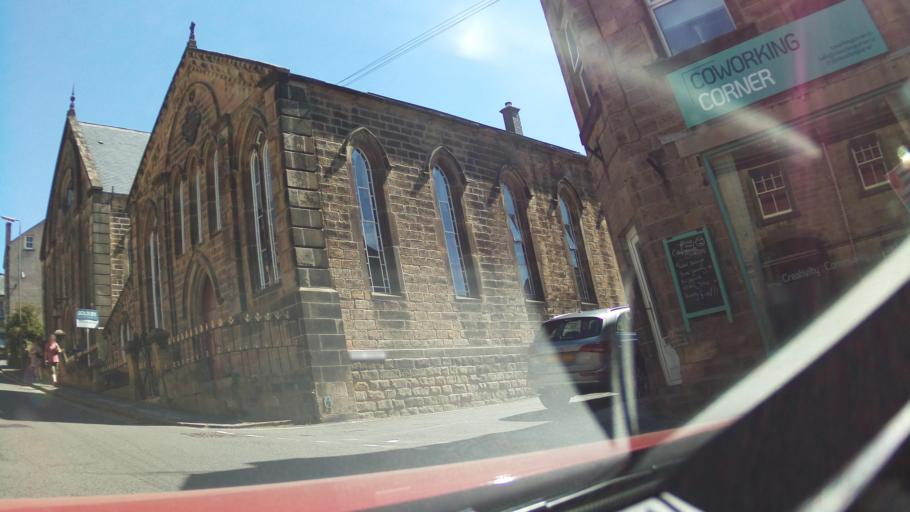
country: GB
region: England
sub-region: Derbyshire
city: Matlock
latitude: 53.1416
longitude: -1.5513
